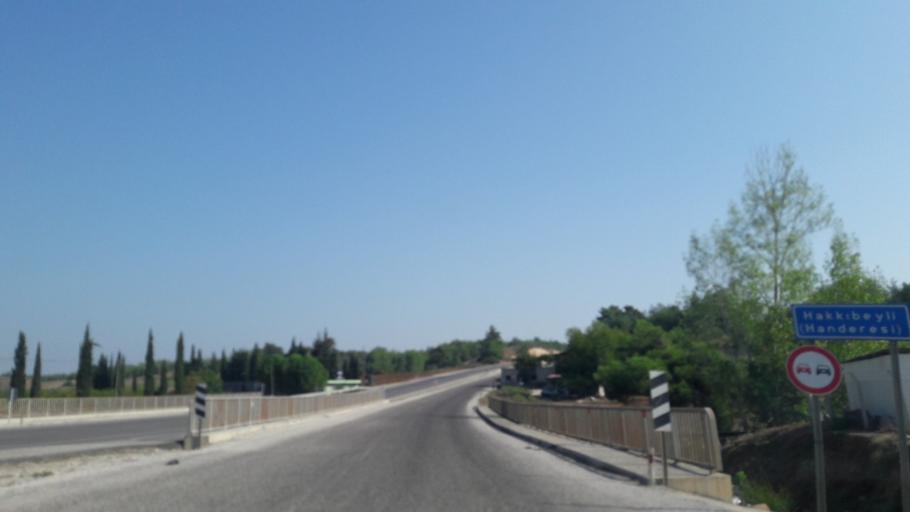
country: TR
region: Adana
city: Sagkaya
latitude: 37.1762
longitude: 35.5658
